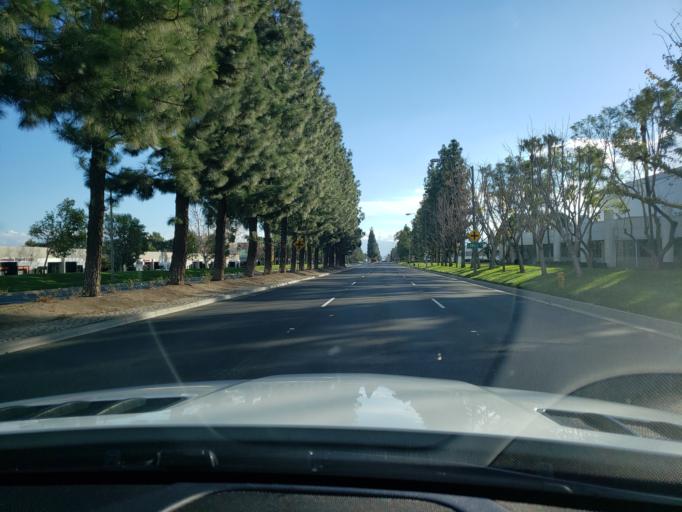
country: US
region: California
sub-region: San Bernardino County
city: Rancho Cucamonga
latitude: 34.0538
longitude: -117.5583
